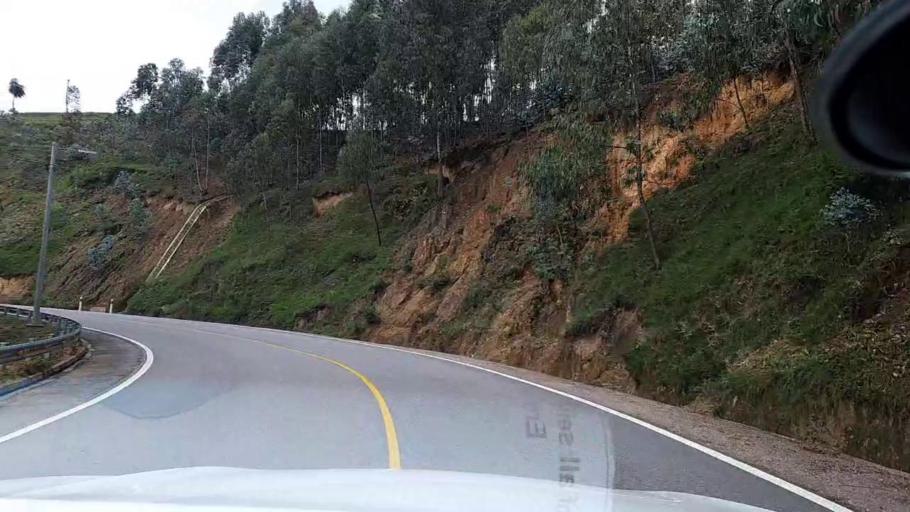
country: RW
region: Southern Province
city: Nzega
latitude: -2.5181
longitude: 29.4591
